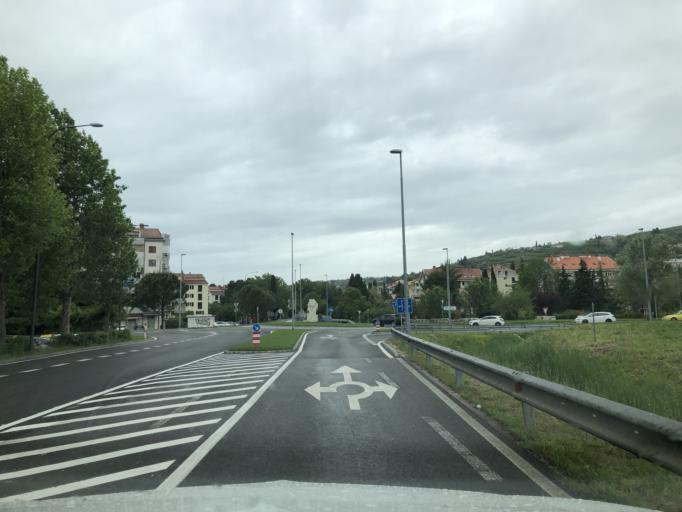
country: SI
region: Piran-Pirano
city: Lucija
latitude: 45.5031
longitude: 13.6066
